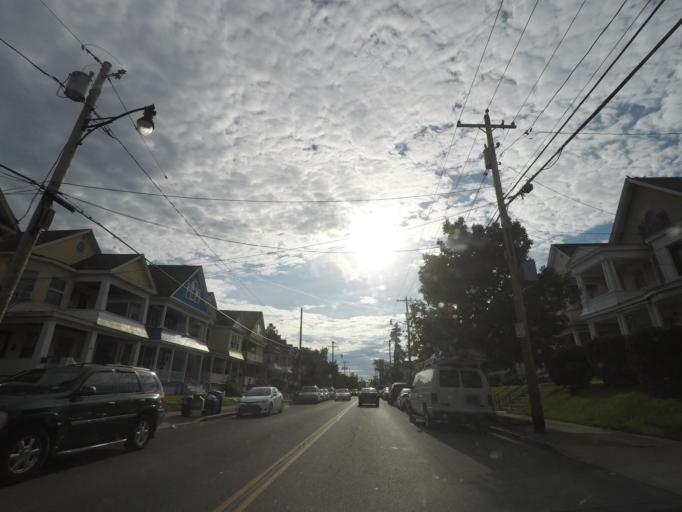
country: US
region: New York
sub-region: Albany County
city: Albany
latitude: 42.6445
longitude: -73.7732
